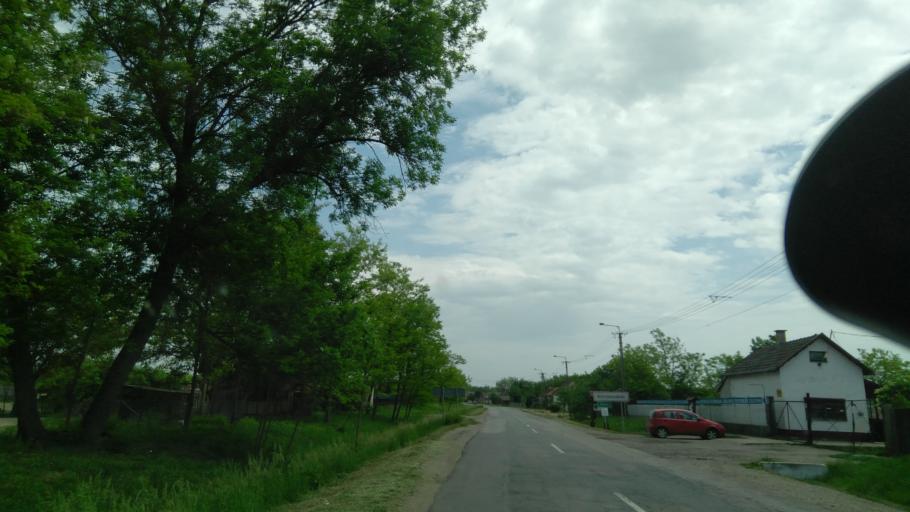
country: HU
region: Hajdu-Bihar
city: Komadi
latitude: 47.0185
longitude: 21.5839
